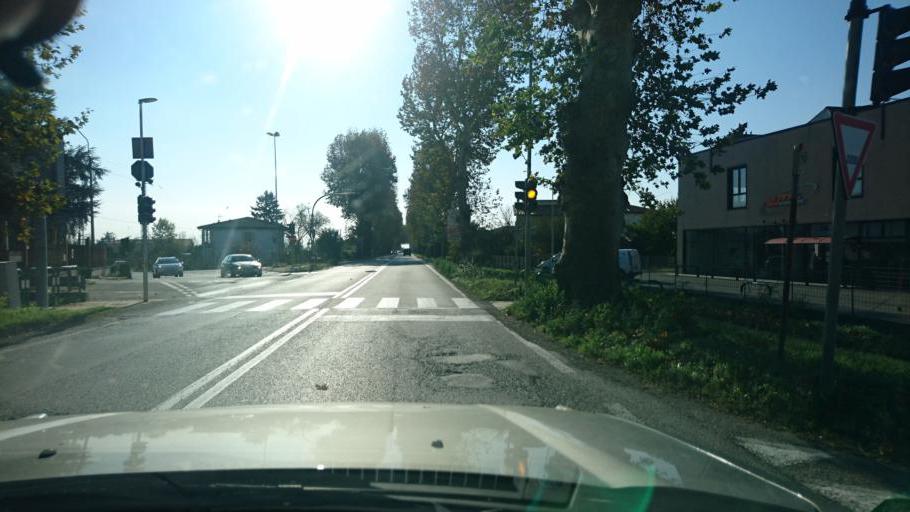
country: IT
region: Veneto
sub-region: Provincia di Padova
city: Monselice
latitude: 45.2298
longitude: 11.7549
